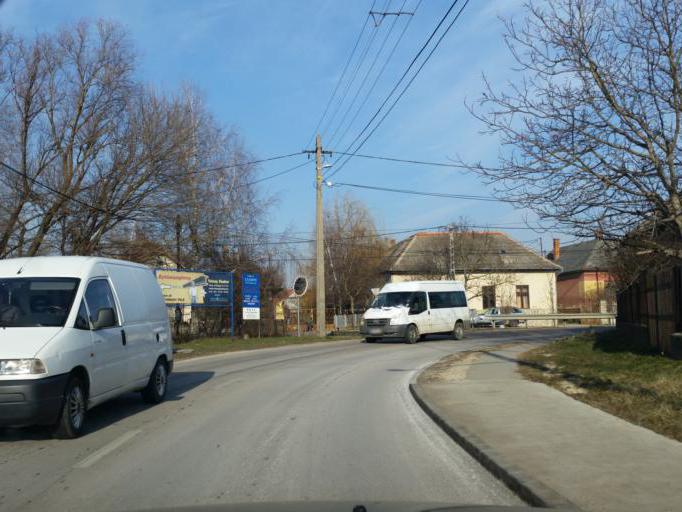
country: HU
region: Pest
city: Paty
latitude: 47.5103
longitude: 18.8233
